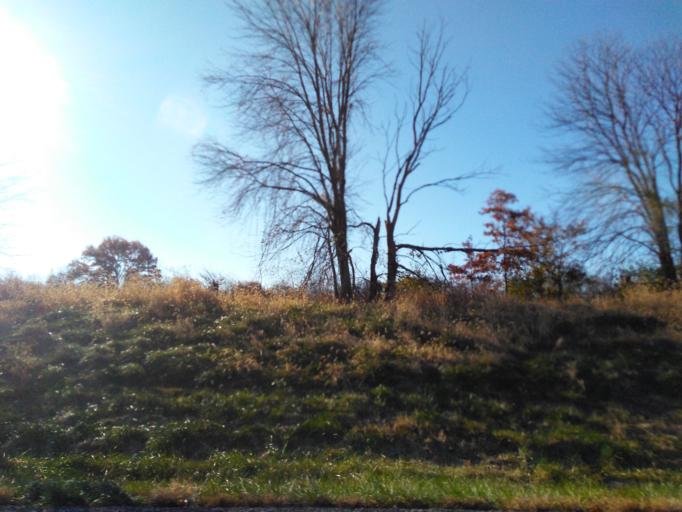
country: US
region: Illinois
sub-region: Madison County
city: Saint Jacob
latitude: 38.7624
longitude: -89.8181
